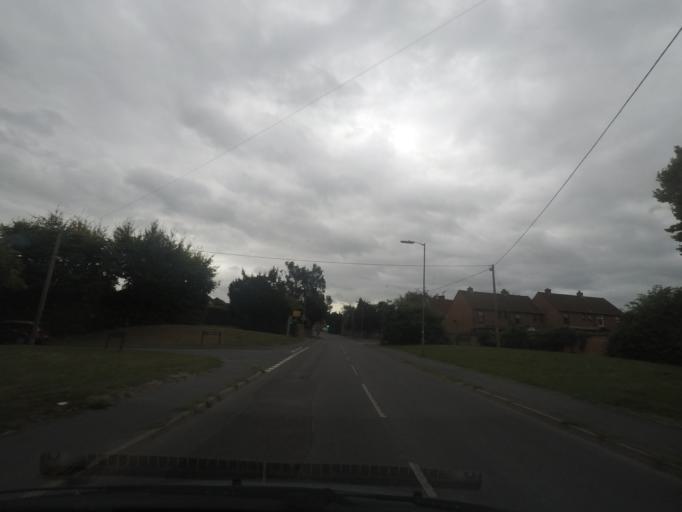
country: GB
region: England
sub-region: Oxfordshire
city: Didcot
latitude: 51.6091
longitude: -1.2528
